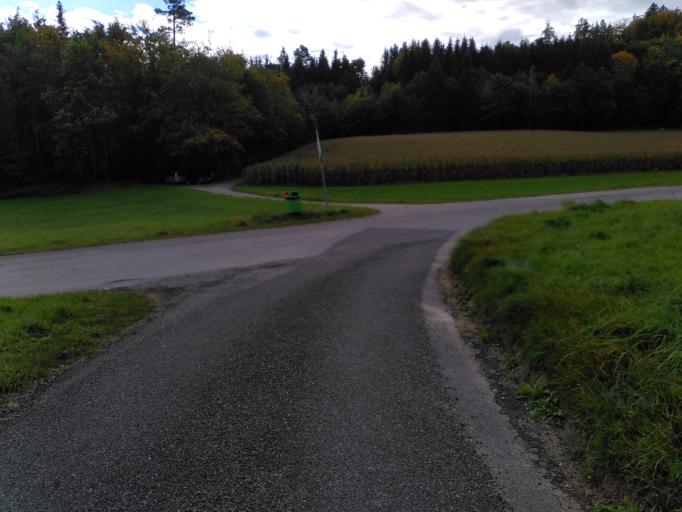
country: CH
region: Bern
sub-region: Emmental District
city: Ersigen
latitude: 47.0947
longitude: 7.6218
